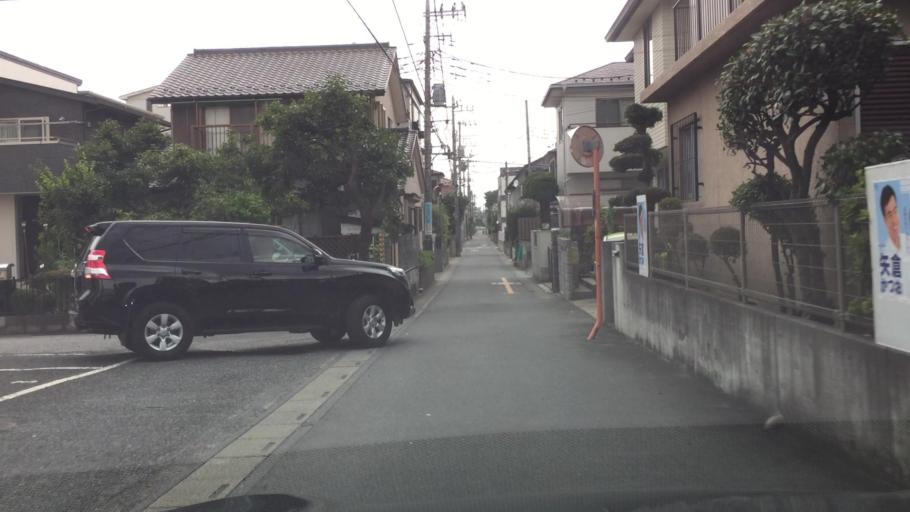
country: JP
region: Saitama
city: Yono
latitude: 35.9154
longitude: 139.6121
